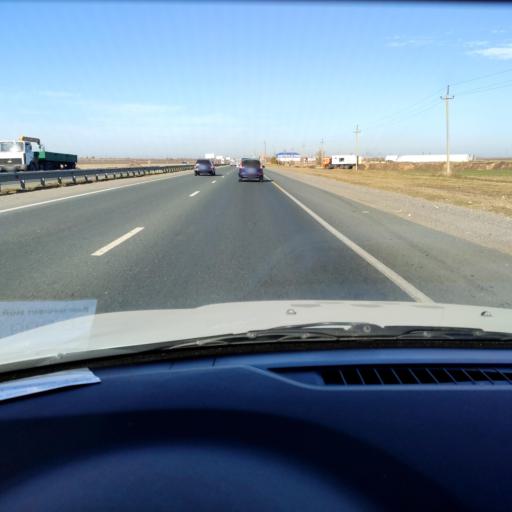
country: RU
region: Samara
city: Zhigulevsk
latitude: 53.5516
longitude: 49.5064
